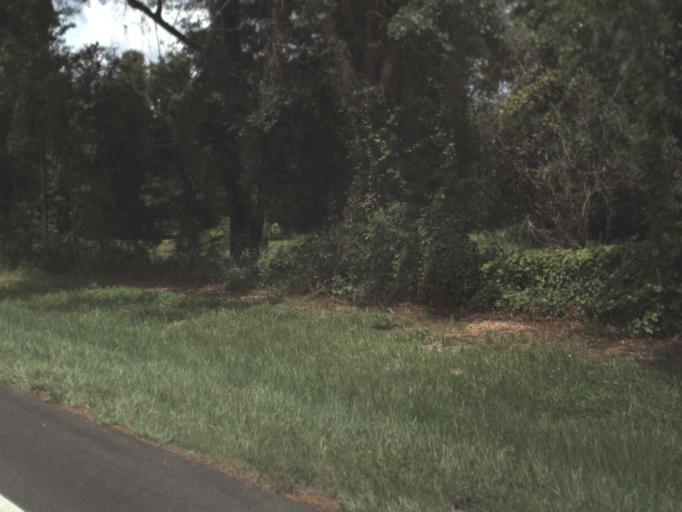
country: US
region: Florida
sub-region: Levy County
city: Williston
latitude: 29.4046
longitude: -82.4512
